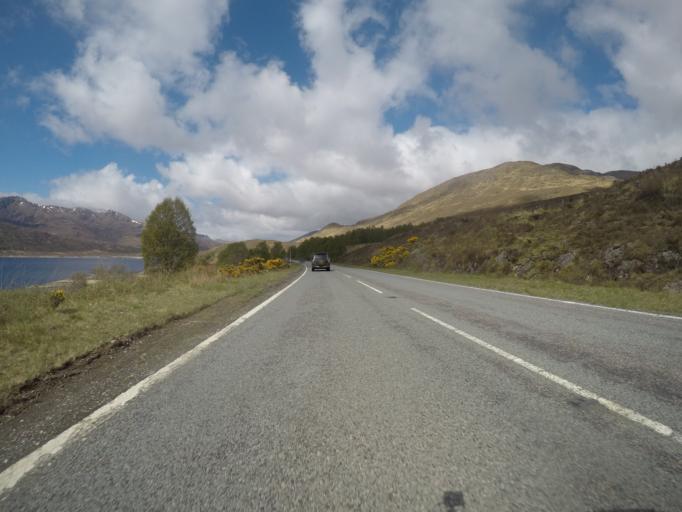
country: GB
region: Scotland
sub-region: Highland
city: Spean Bridge
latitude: 57.1470
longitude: -5.0950
